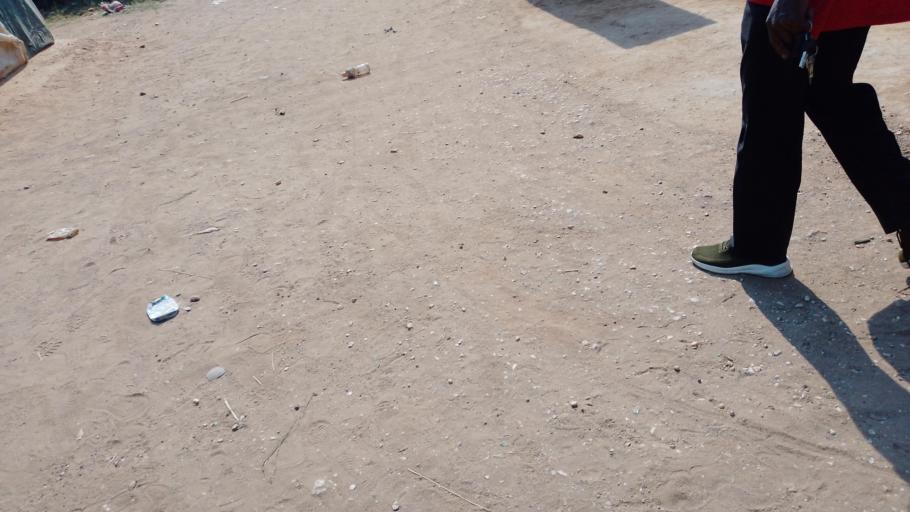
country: ZM
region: Lusaka
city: Lusaka
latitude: -15.3961
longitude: 28.3722
